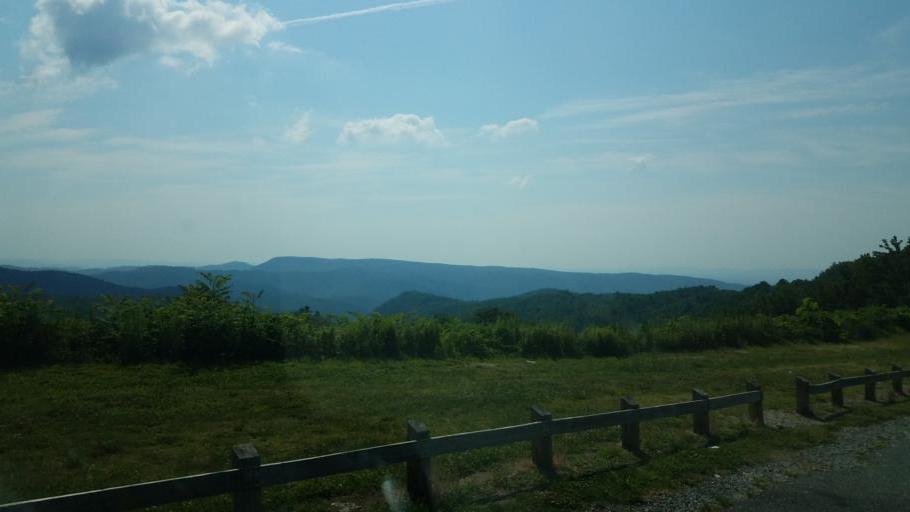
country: US
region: North Carolina
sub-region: Avery County
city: Newland
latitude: 35.9425
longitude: -81.8422
